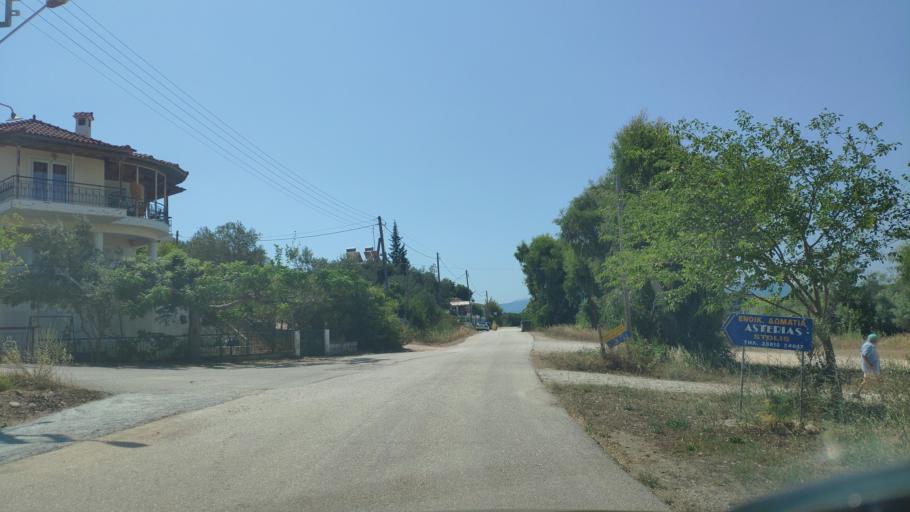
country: GR
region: Epirus
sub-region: Nomos Artas
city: Aneza
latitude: 39.0131
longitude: 20.9182
